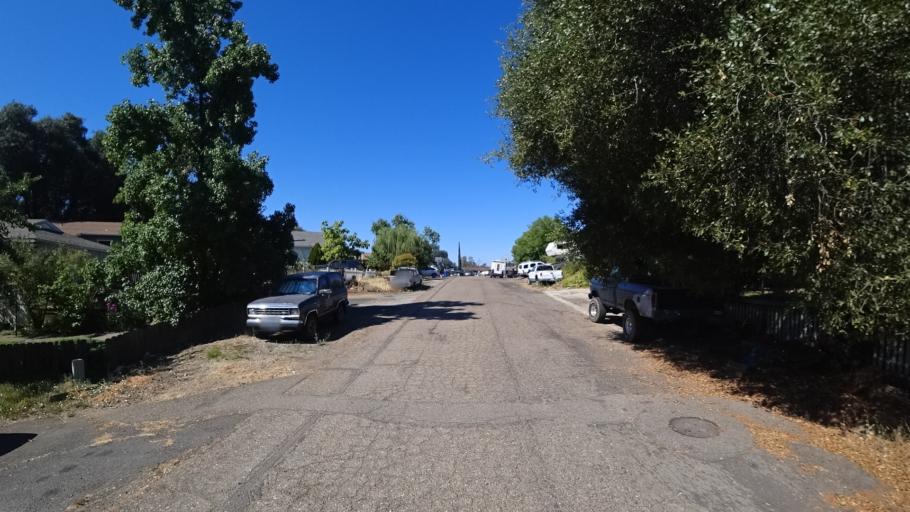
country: US
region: California
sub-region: Calaveras County
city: Murphys
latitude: 38.1095
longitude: -120.4580
